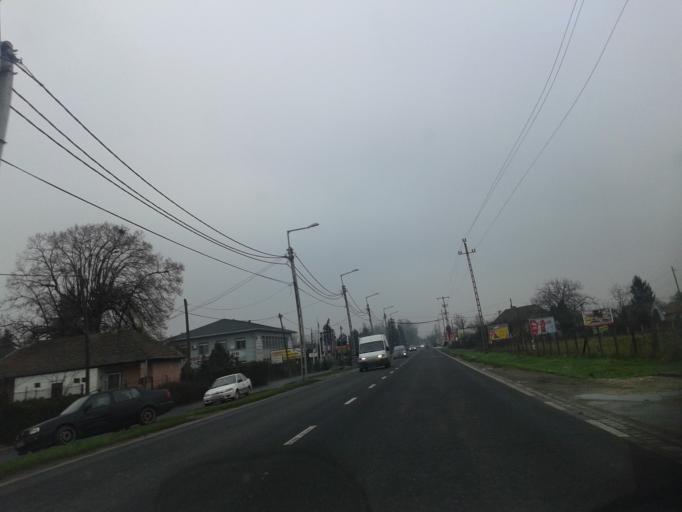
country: HU
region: Budapest
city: Budapest XXII. keruelet
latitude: 47.3942
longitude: 19.0409
